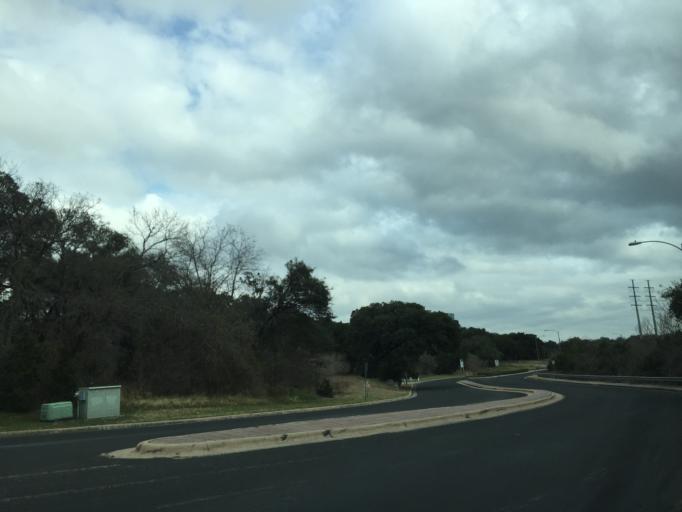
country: US
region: Texas
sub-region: Travis County
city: Wells Branch
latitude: 30.3924
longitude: -97.6752
